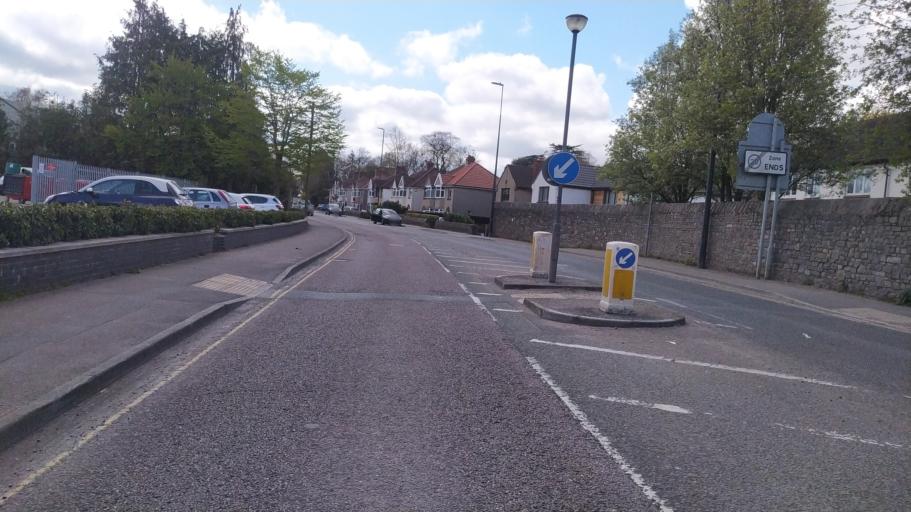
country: GB
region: England
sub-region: South Gloucestershire
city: Siston
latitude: 51.4562
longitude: -2.4763
